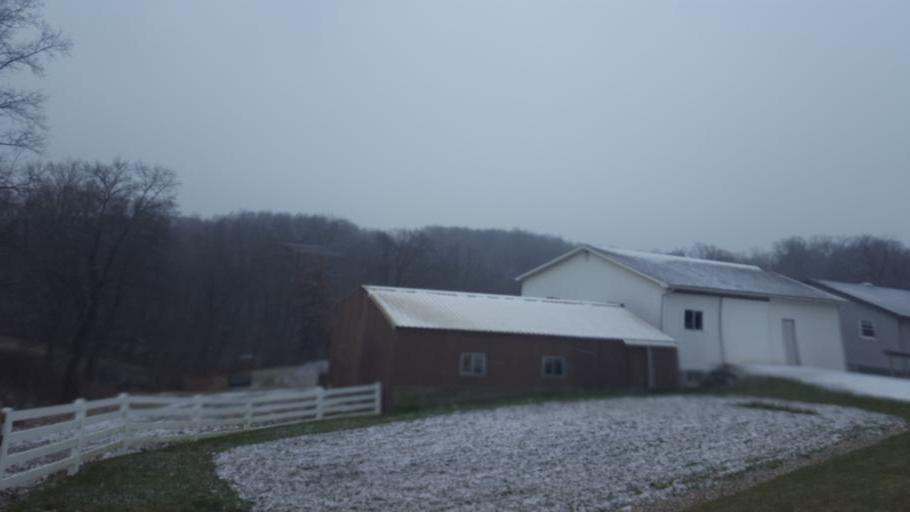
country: US
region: Ohio
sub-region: Tuscarawas County
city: Sugarcreek
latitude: 40.4359
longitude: -81.7694
